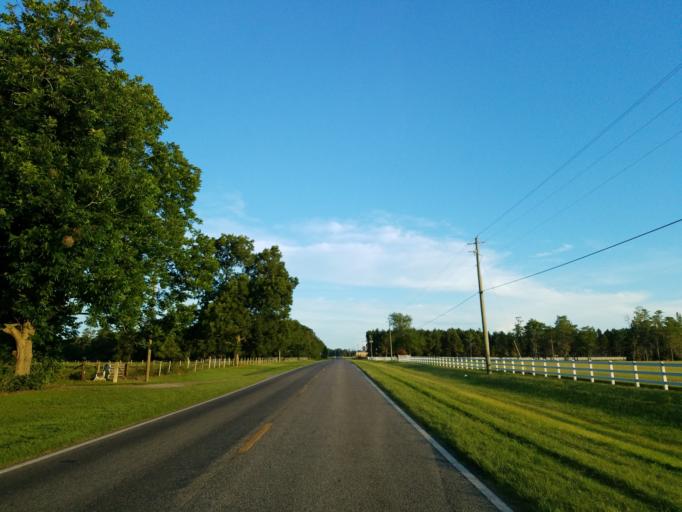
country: US
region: Georgia
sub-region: Cook County
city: Sparks
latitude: 31.1965
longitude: -83.4481
